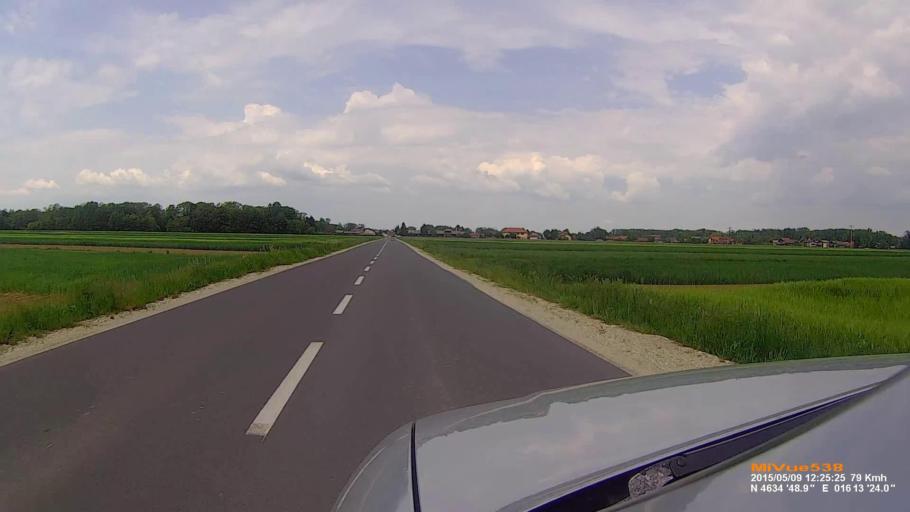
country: SI
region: Beltinci
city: Beltinci
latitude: 46.5802
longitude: 16.2234
